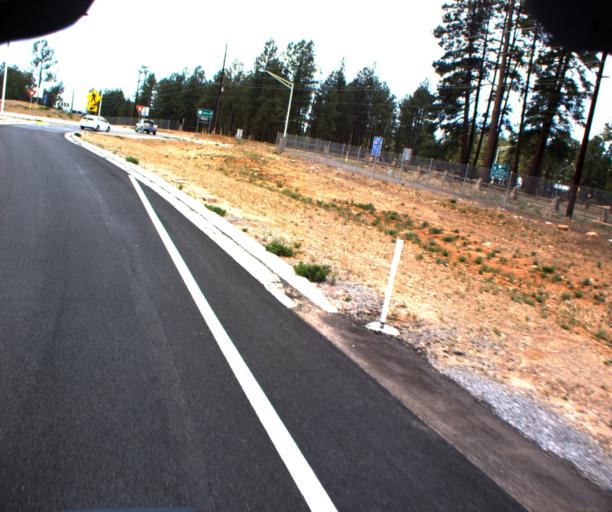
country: US
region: Arizona
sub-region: Coconino County
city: Kachina Village
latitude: 35.1407
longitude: -111.6856
